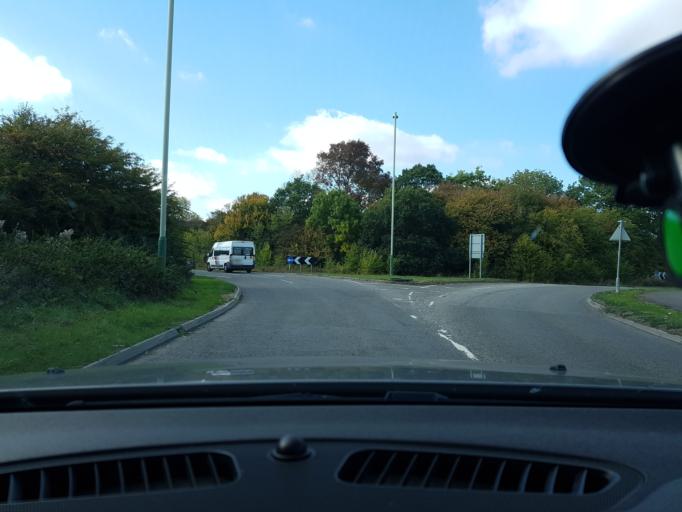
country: GB
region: England
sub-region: Borough of Swindon
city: Wanborough
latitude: 51.5397
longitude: -1.7209
